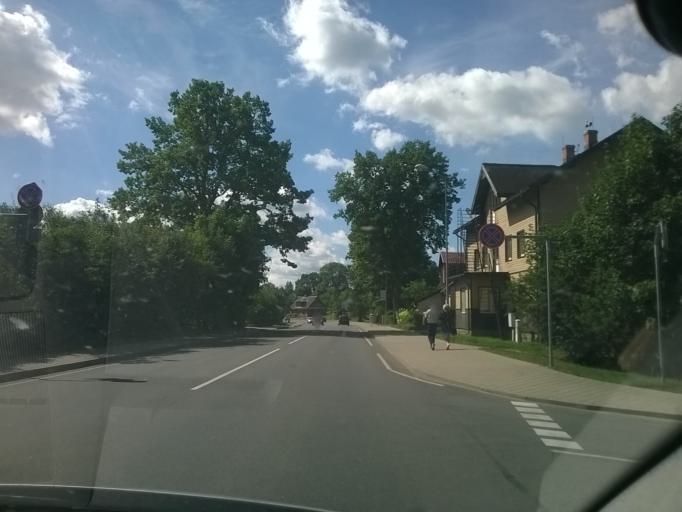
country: LV
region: Aluksnes Rajons
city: Aluksne
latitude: 57.4313
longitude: 27.0395
